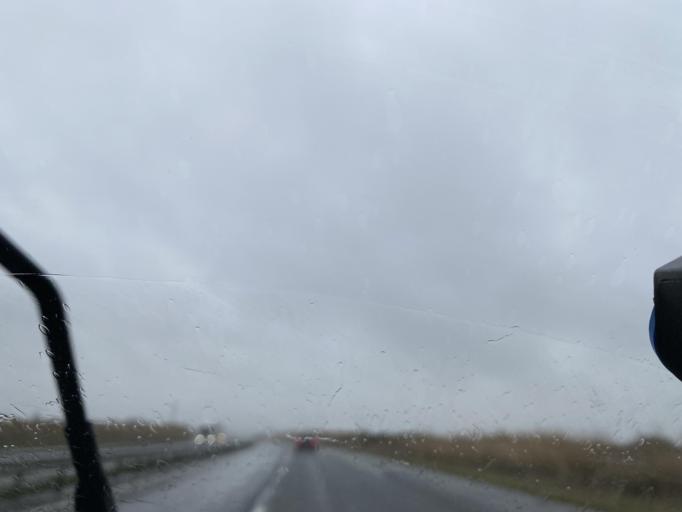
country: FR
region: Centre
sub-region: Departement d'Eure-et-Loir
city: Bailleau-l'Eveque
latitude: 48.5392
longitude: 1.4506
